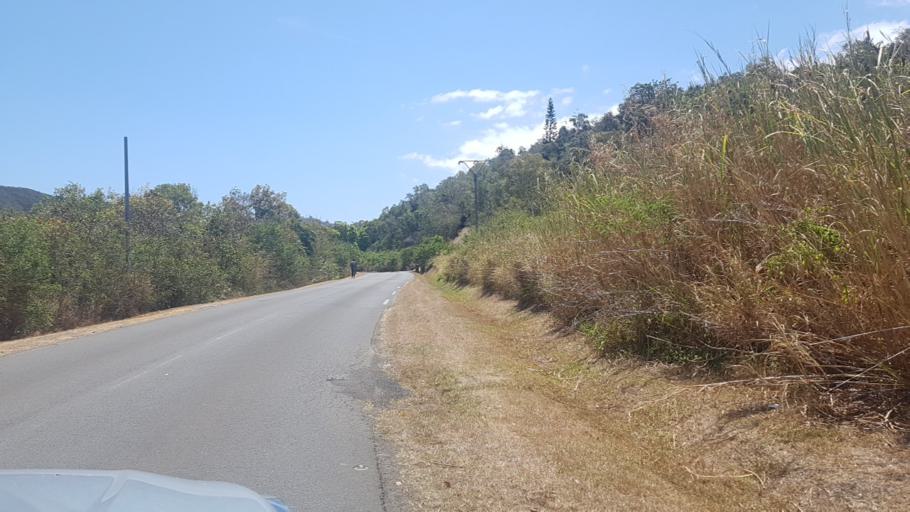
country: NC
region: South Province
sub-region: Dumbea
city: Dumbea
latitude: -22.1394
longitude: 166.4419
